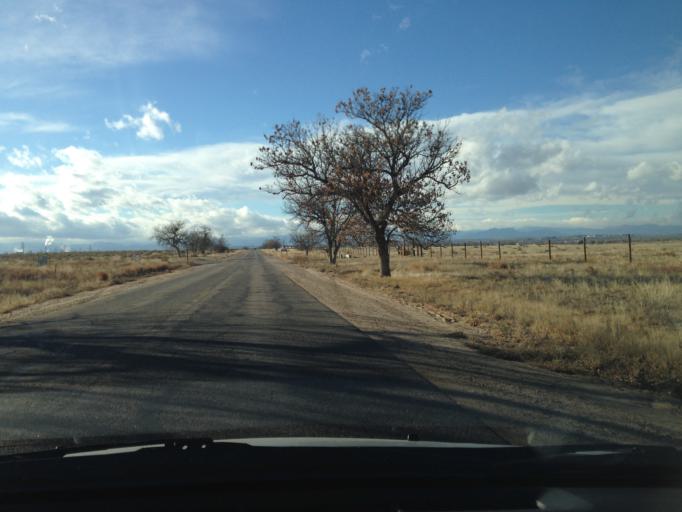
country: US
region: Colorado
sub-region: Adams County
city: Derby
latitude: 39.8273
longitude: -104.8831
